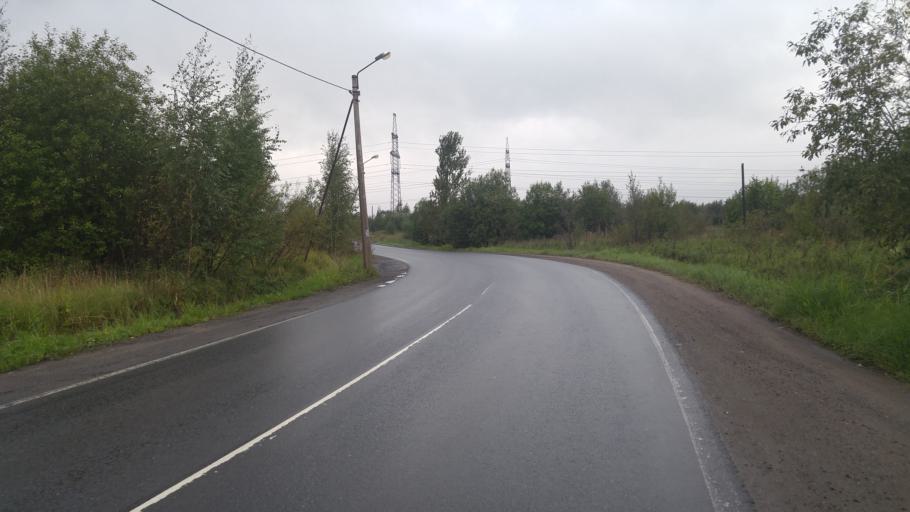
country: RU
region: St.-Petersburg
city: Metallostroy
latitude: 59.8037
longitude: 30.5412
